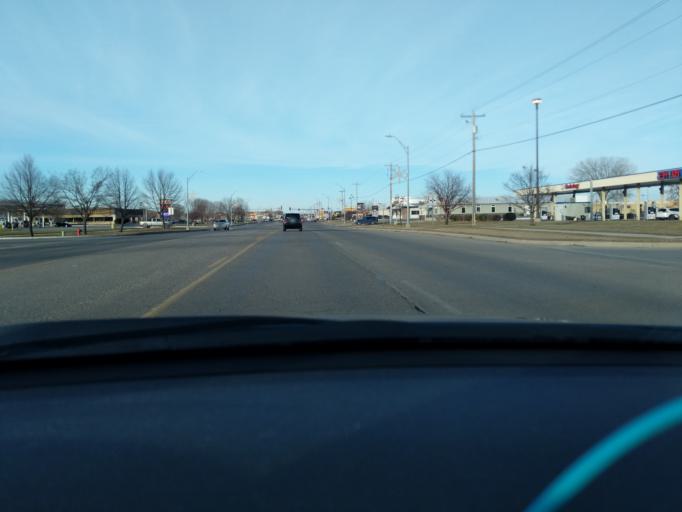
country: US
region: Minnesota
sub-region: Kandiyohi County
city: Willmar
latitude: 45.1010
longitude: -95.0426
